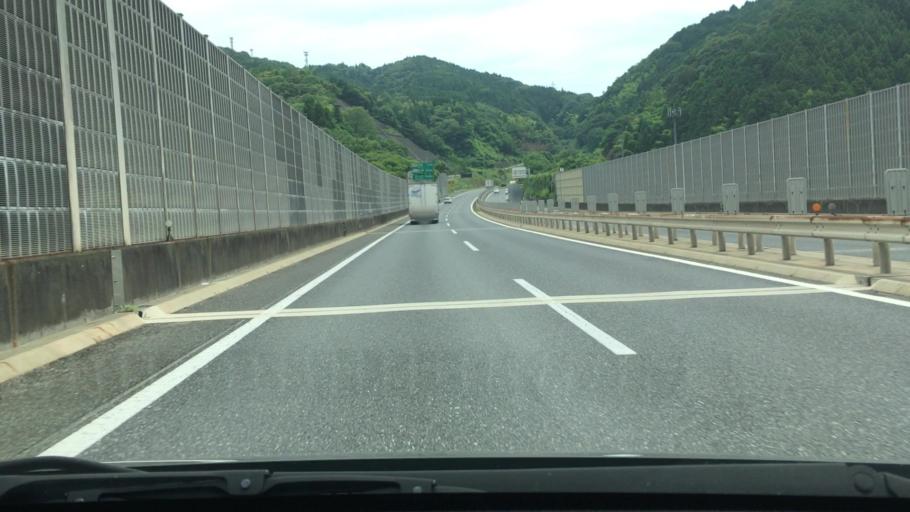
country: JP
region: Yamaguchi
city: Otake
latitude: 34.2360
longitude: 132.2138
